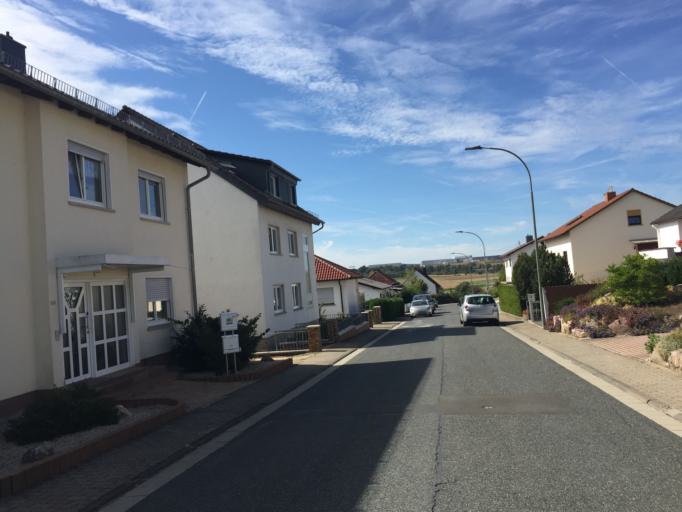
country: DE
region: Hesse
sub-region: Regierungsbezirk Giessen
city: Langgons
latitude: 50.4744
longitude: 8.6697
